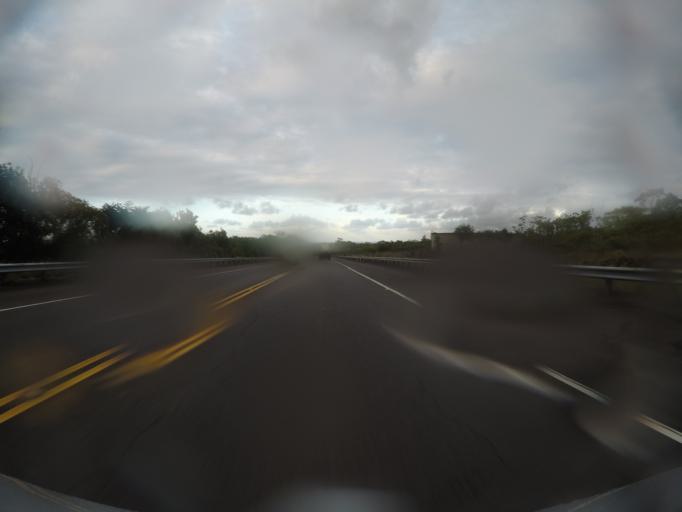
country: US
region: Hawaii
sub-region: Hawaii County
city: Hilo
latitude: 19.6929
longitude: -155.1060
